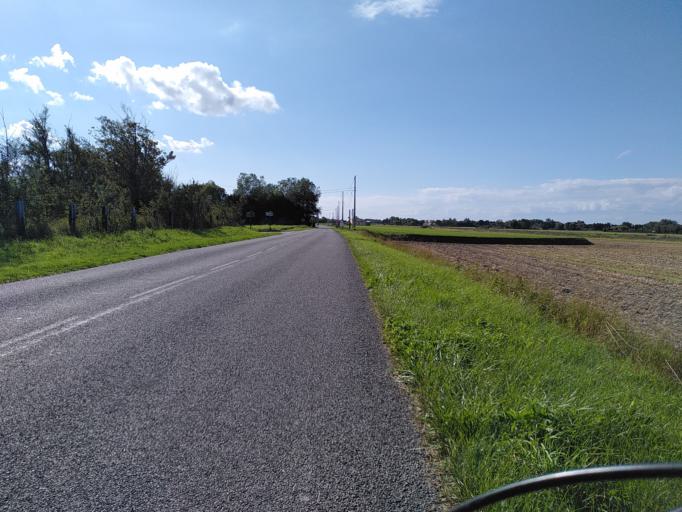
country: FR
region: Nord-Pas-de-Calais
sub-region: Departement du Pas-de-Calais
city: Oye-Plage
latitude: 50.9879
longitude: 2.0101
